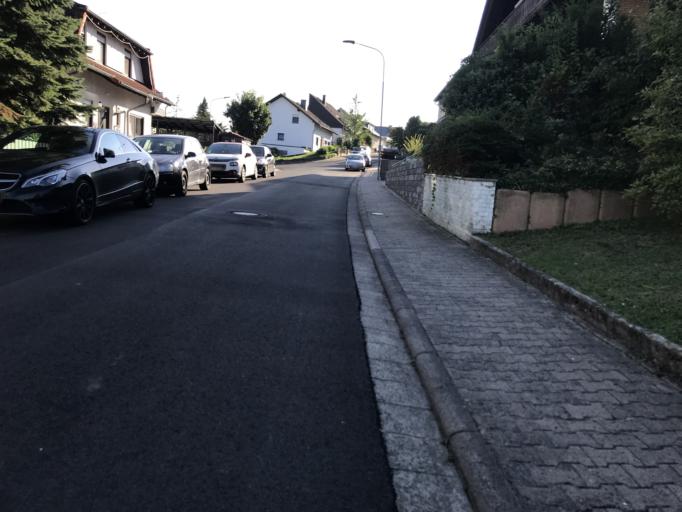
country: DE
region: Hesse
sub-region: Regierungsbezirk Darmstadt
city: Altenstadt
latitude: 50.2625
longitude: 8.9101
